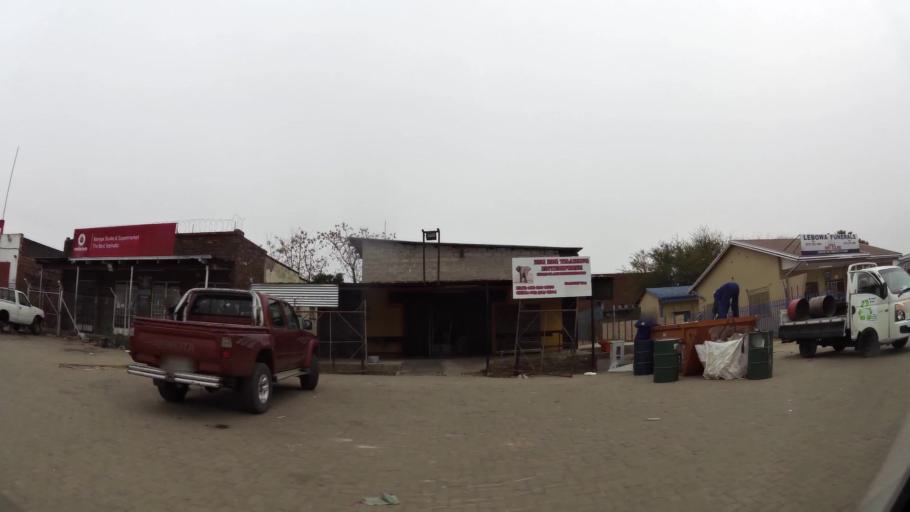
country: ZA
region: Limpopo
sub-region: Capricorn District Municipality
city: Polokwane
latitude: -23.8474
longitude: 29.3909
